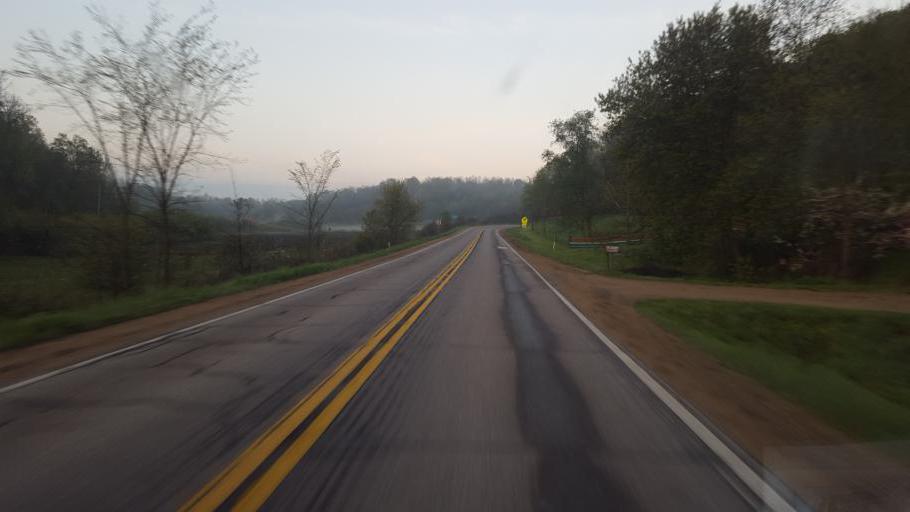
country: US
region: Wisconsin
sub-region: Vernon County
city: Hillsboro
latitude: 43.6416
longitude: -90.4399
